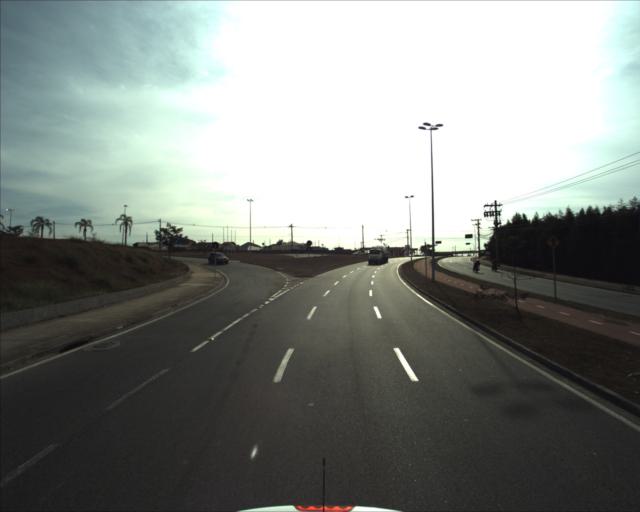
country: BR
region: Sao Paulo
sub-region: Sorocaba
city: Sorocaba
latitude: -23.4560
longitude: -47.4517
